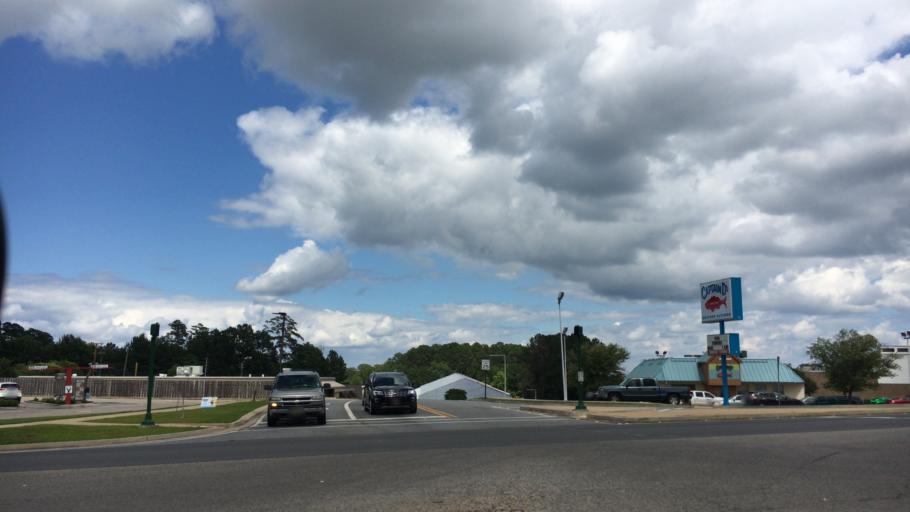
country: US
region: Louisiana
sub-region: Lincoln Parish
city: Ruston
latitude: 32.5433
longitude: -92.6395
